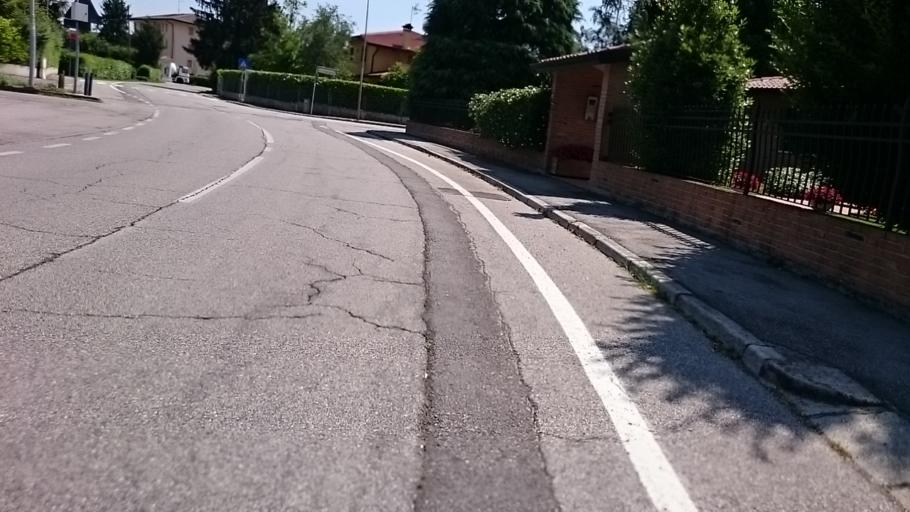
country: IT
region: Veneto
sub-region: Provincia di Padova
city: San Vito
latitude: 45.4217
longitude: 11.9590
